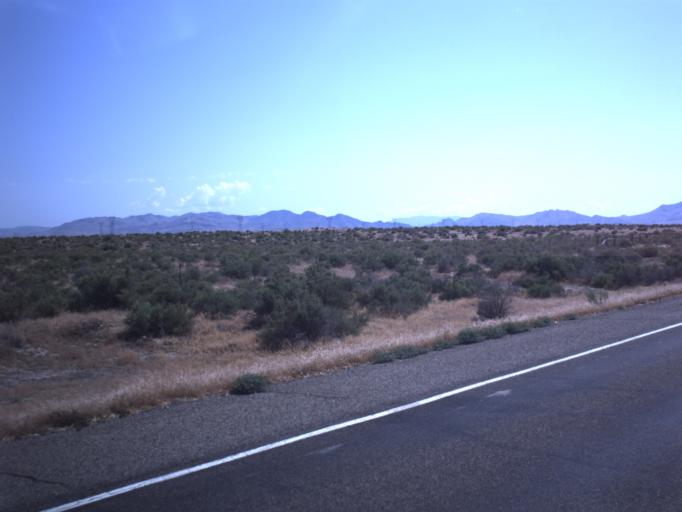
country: US
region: Utah
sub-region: Millard County
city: Delta
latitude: 39.4821
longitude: -112.5178
